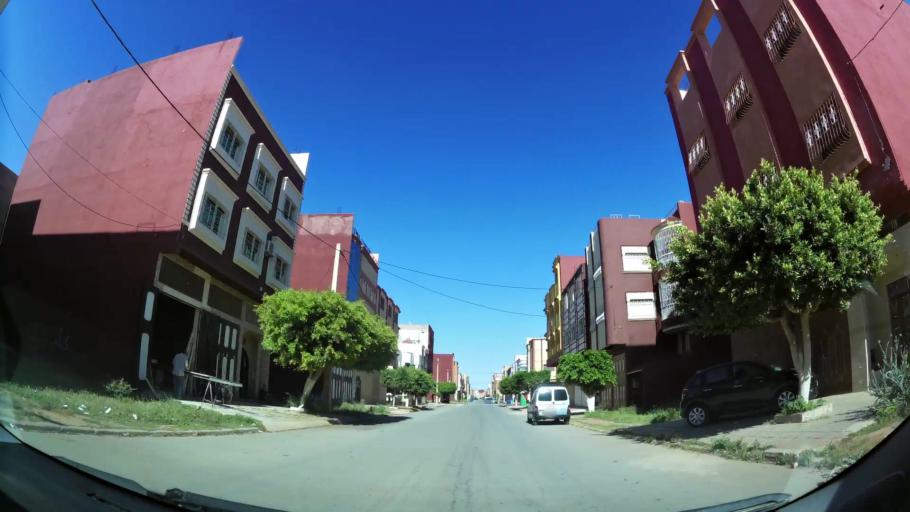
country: MA
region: Oriental
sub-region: Berkane-Taourirt
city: Berkane
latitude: 34.9365
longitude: -2.3356
